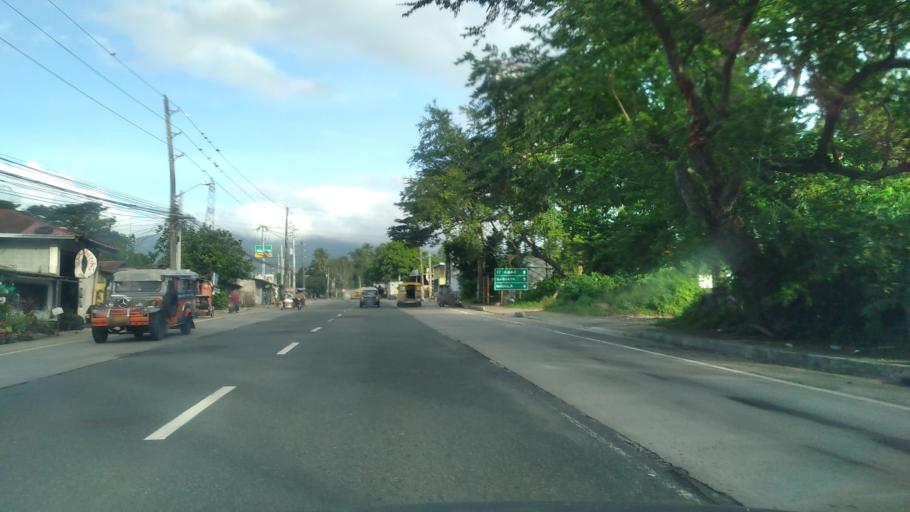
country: PH
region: Calabarzon
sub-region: Province of Quezon
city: Isabang
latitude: 13.9695
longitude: 121.5624
